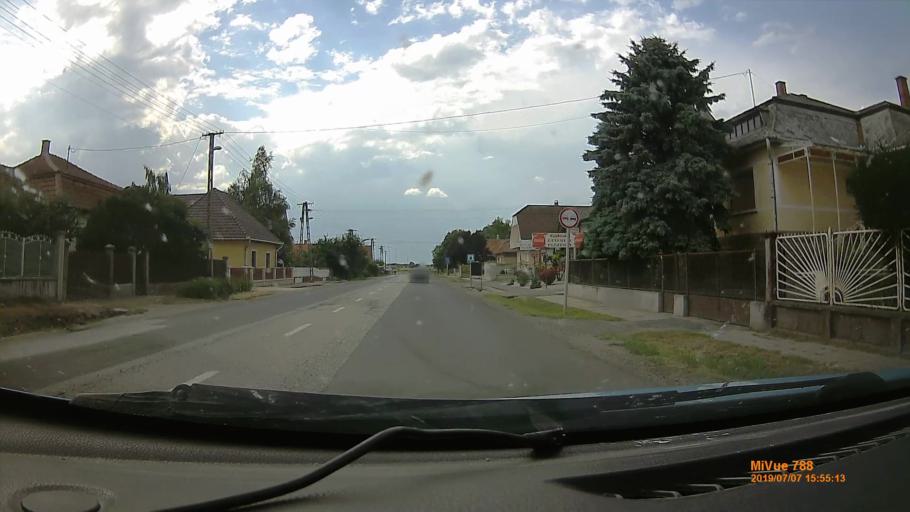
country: HU
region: Pest
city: Szentlorinckata
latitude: 47.5580
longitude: 19.7885
